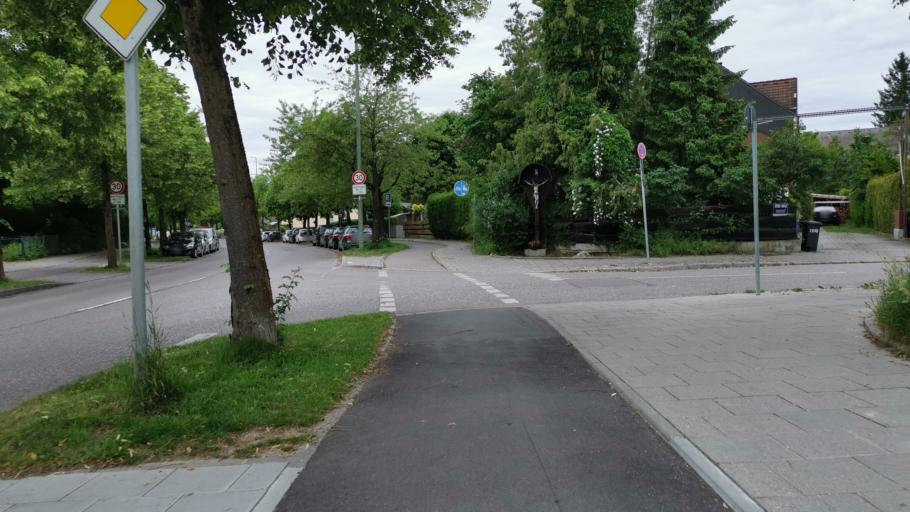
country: DE
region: Bavaria
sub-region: Upper Bavaria
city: Neuried
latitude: 48.0870
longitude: 11.4982
